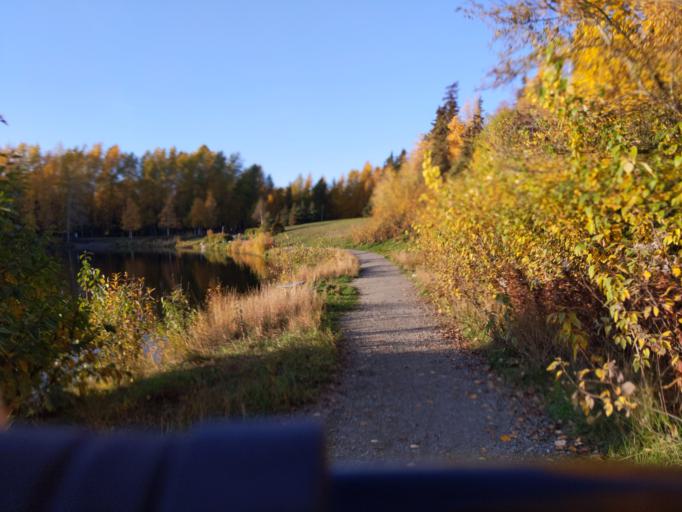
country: US
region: Alaska
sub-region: Anchorage Municipality
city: Anchorage
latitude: 61.1505
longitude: -149.8795
